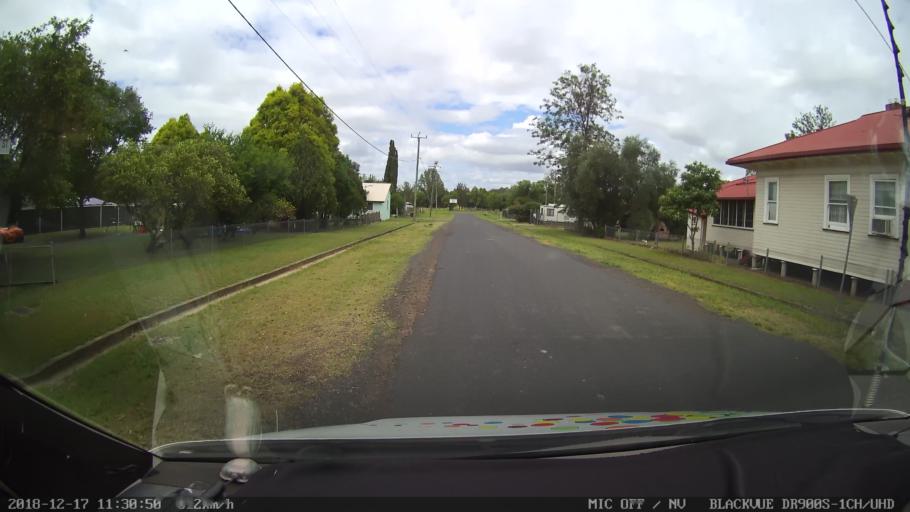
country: AU
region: New South Wales
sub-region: Kyogle
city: Kyogle
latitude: -28.7379
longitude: 152.6226
